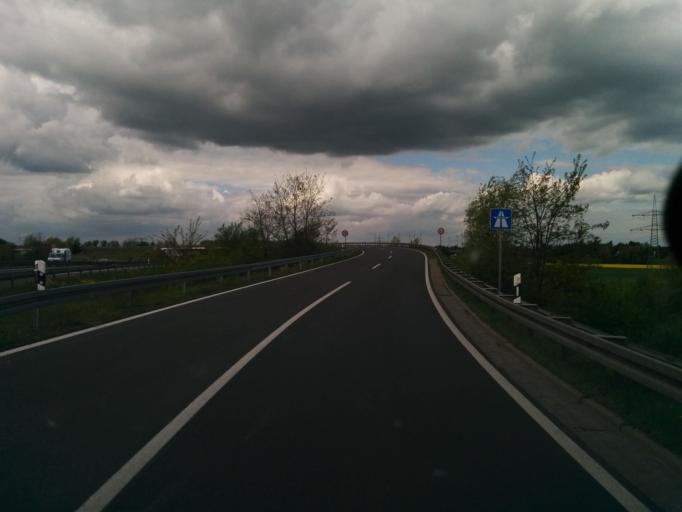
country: DE
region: Brandenburg
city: Wustermark
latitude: 52.5404
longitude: 12.9726
